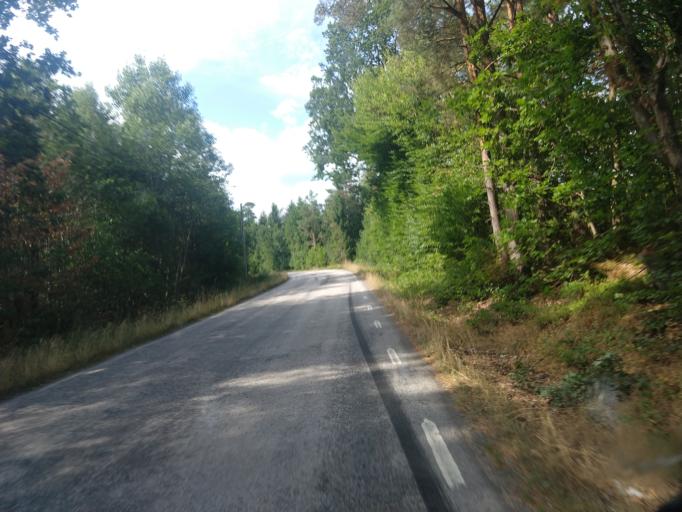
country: SE
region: Blekinge
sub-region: Karlskrona Kommun
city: Rodeby
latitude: 56.2346
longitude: 15.5765
